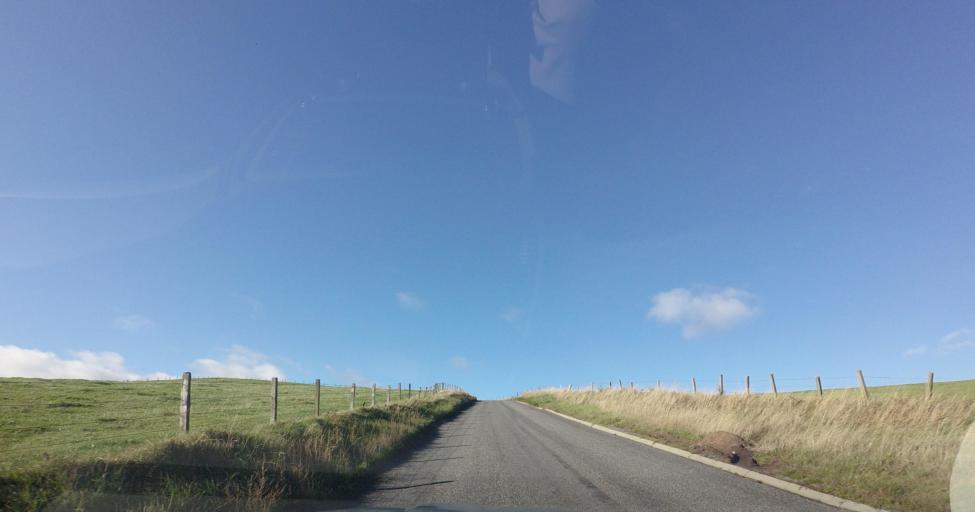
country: GB
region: Scotland
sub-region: Aberdeenshire
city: Rosehearty
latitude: 57.6795
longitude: -2.2755
